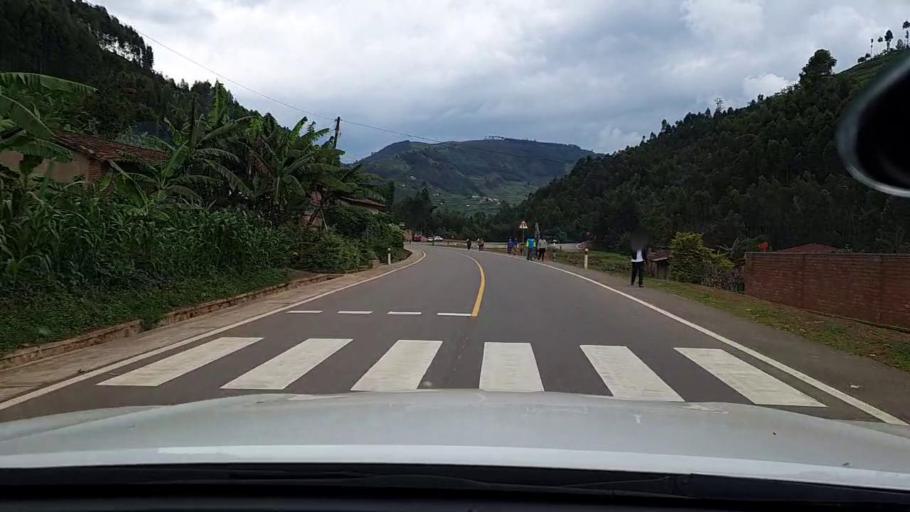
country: RW
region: Northern Province
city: Byumba
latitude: -1.6279
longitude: 29.9266
